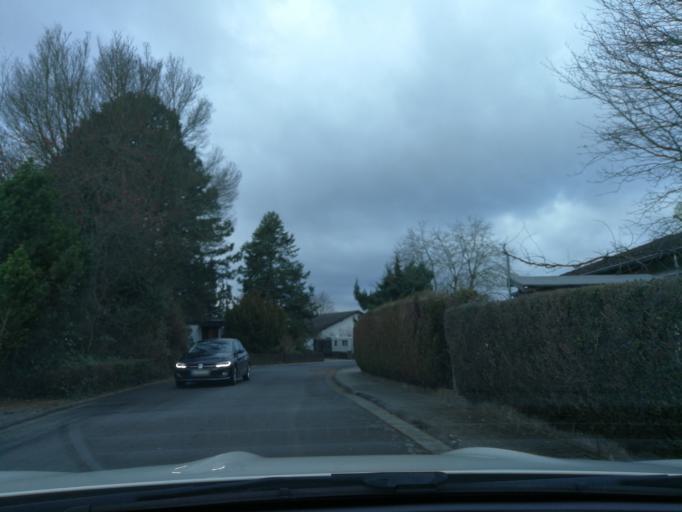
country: DE
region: Hesse
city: Reinheim
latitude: 49.8281
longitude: 8.8260
